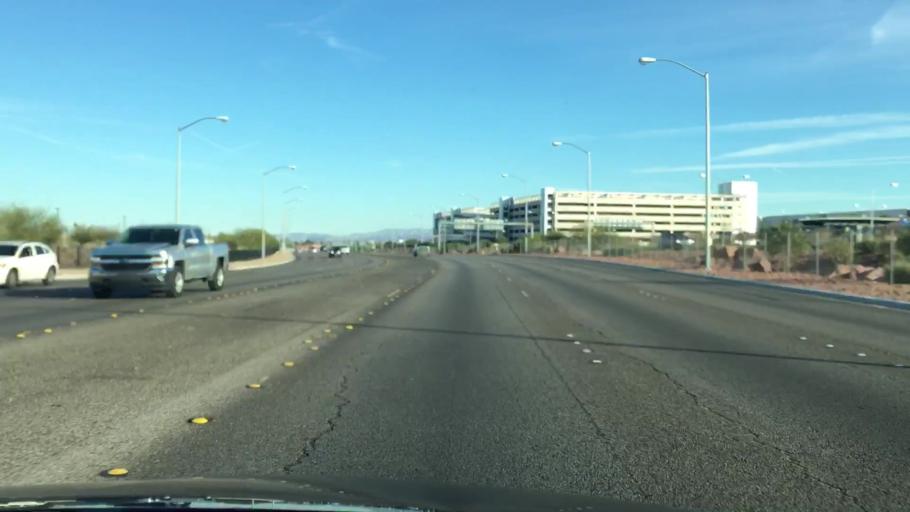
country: US
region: Nevada
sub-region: Clark County
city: Paradise
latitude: 36.0891
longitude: -115.1427
